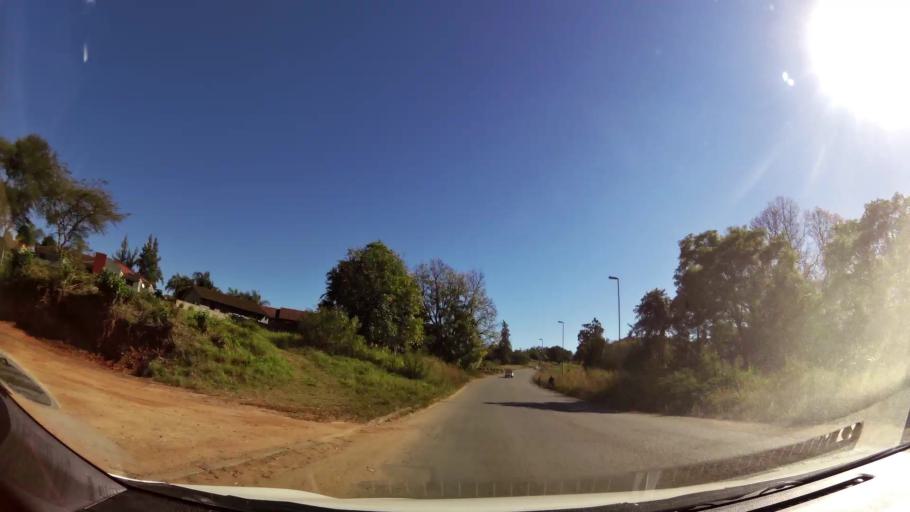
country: ZA
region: Limpopo
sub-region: Mopani District Municipality
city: Tzaneen
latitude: -23.8490
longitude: 30.1682
